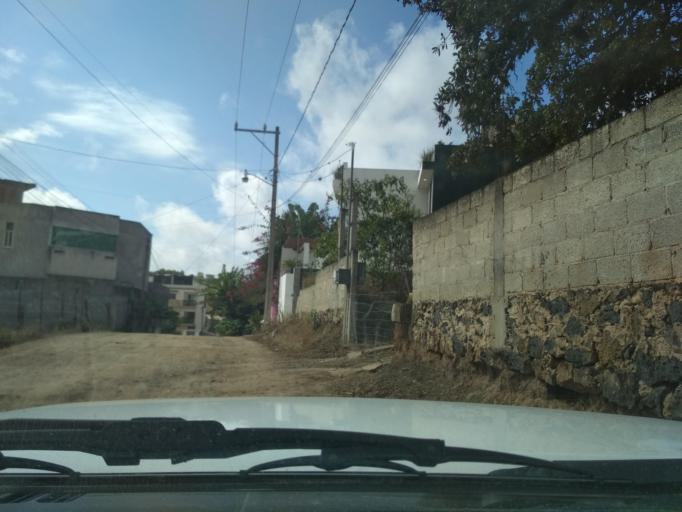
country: MX
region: Veracruz
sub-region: Emiliano Zapata
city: Jacarandas
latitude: 19.4984
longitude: -96.8419
